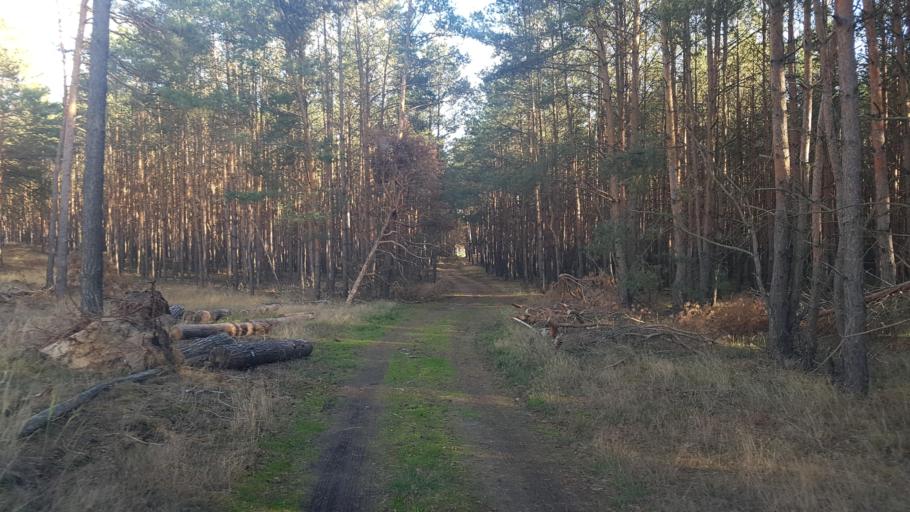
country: DE
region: Brandenburg
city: Herzberg
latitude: 51.6656
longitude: 13.3056
